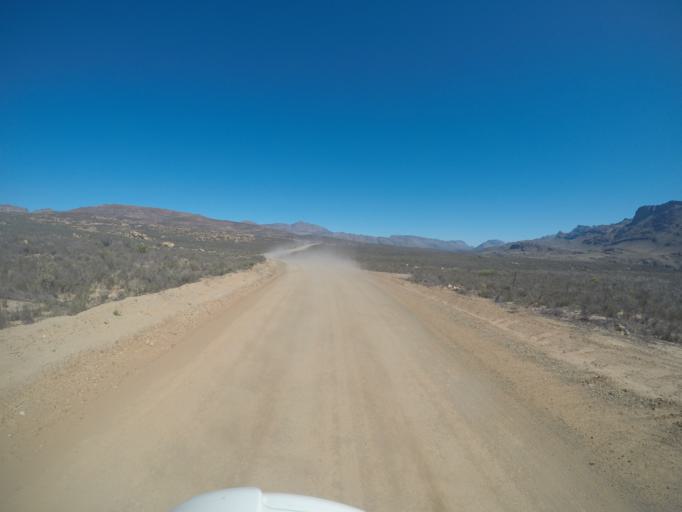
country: ZA
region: Western Cape
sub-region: West Coast District Municipality
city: Clanwilliam
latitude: -32.5053
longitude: 19.2955
